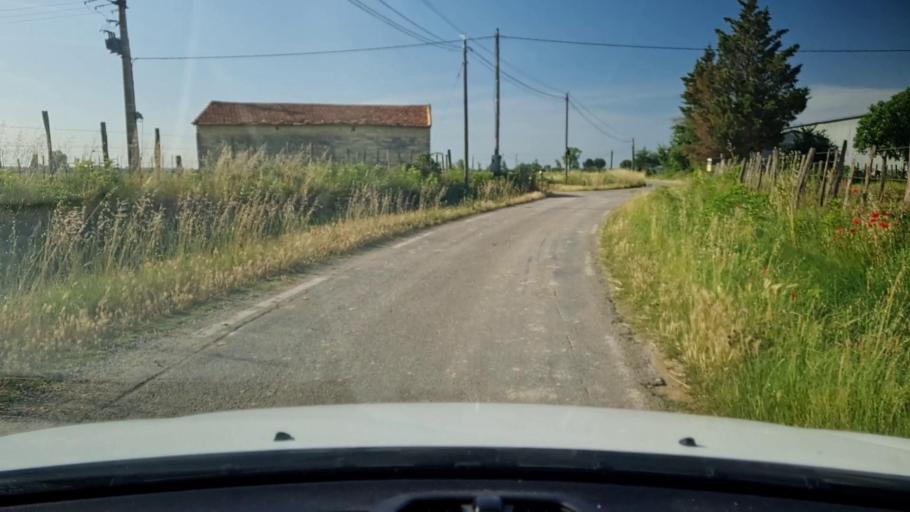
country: FR
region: Languedoc-Roussillon
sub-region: Departement du Gard
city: Le Cailar
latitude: 43.6513
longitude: 4.2190
